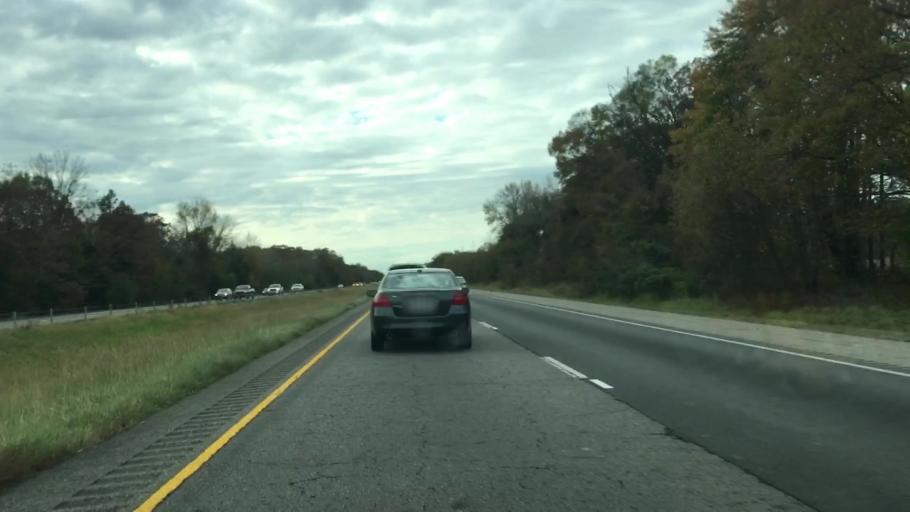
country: US
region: Arkansas
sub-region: Conway County
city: Morrilton
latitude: 35.1609
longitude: -92.5977
